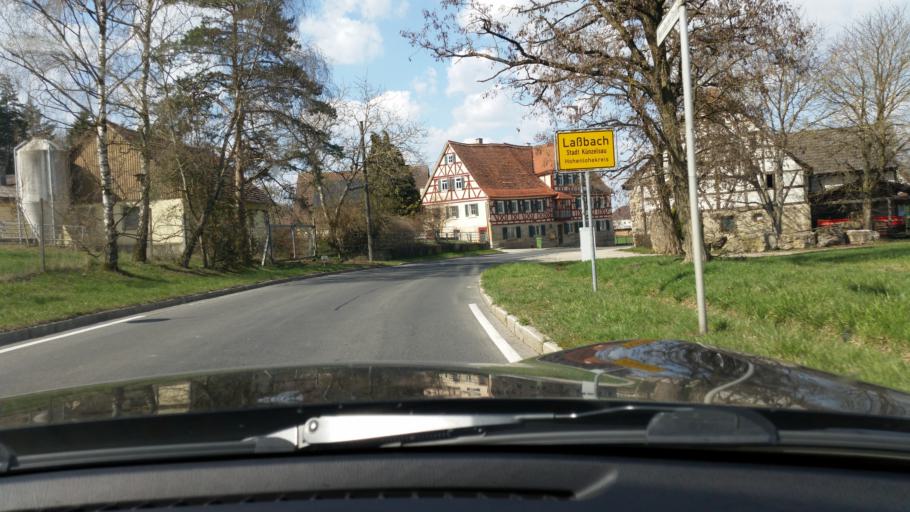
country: DE
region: Baden-Wuerttemberg
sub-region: Regierungsbezirk Stuttgart
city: Langenburg
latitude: 49.2632
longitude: 9.8108
